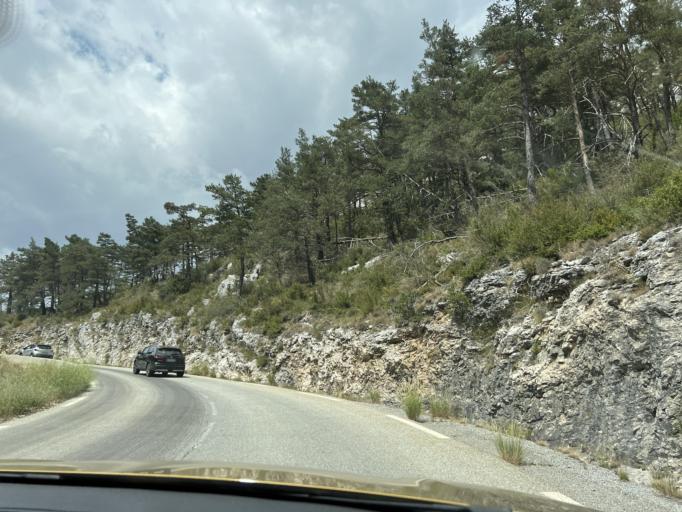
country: FR
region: Provence-Alpes-Cote d'Azur
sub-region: Departement des Alpes-Maritimes
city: Saint-Vallier-de-Thiey
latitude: 43.8016
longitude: 6.9033
